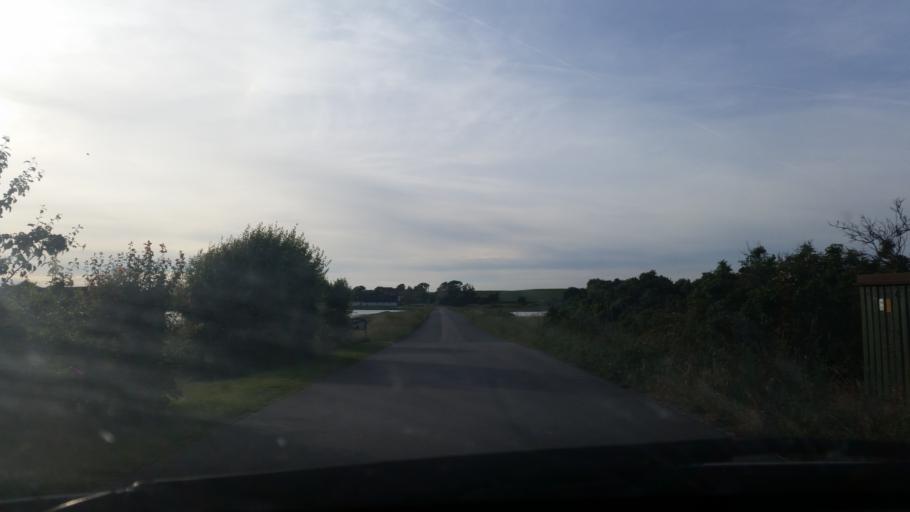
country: DK
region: Central Jutland
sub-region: Samso Kommune
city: Tranebjerg
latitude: 55.9134
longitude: 10.6411
